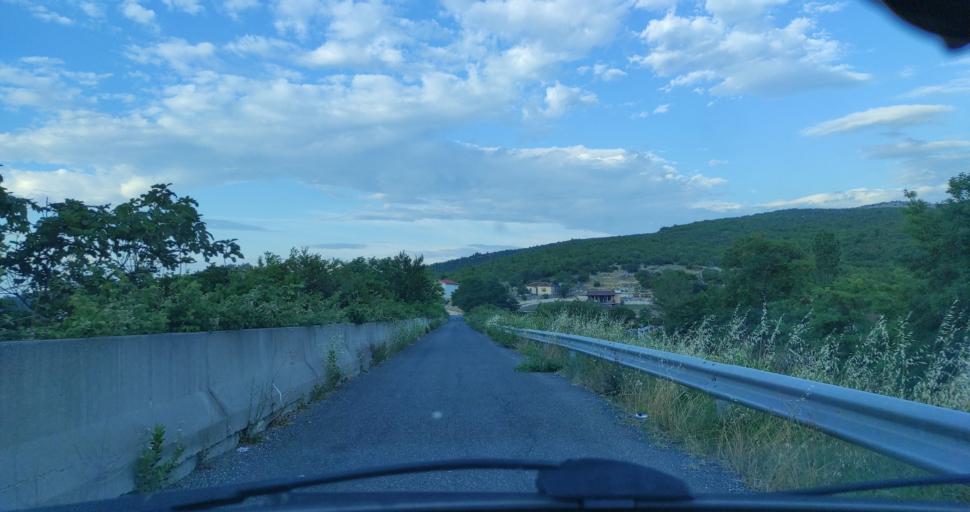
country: AL
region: Shkoder
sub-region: Rrethi i Shkodres
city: Velipoje
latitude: 41.9269
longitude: 19.4672
